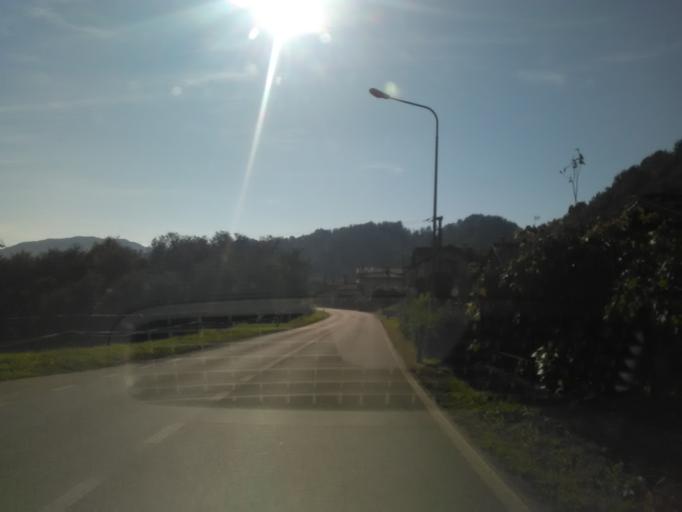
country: IT
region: Piedmont
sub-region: Provincia di Vercelli
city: Postua
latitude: 45.7037
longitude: 8.2337
